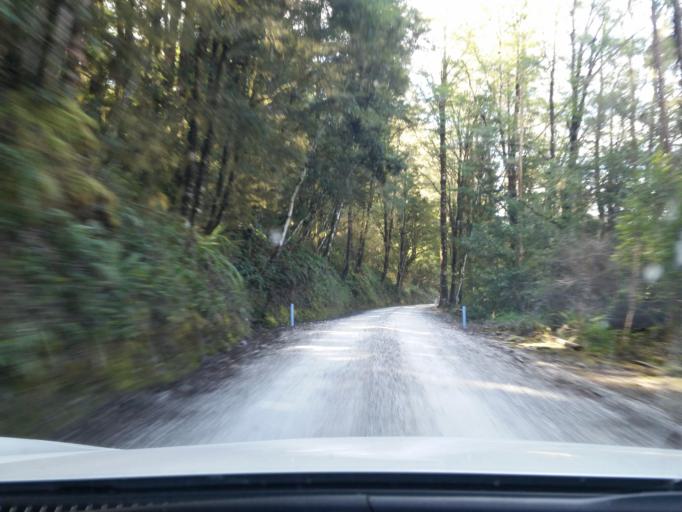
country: NZ
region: West Coast
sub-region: Buller District
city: Westport
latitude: -41.8727
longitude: 172.2466
